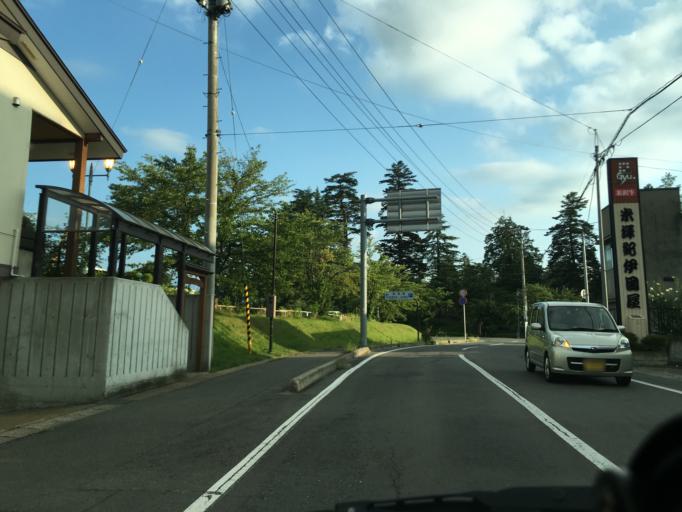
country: JP
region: Yamagata
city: Yonezawa
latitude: 37.9108
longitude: 140.1057
